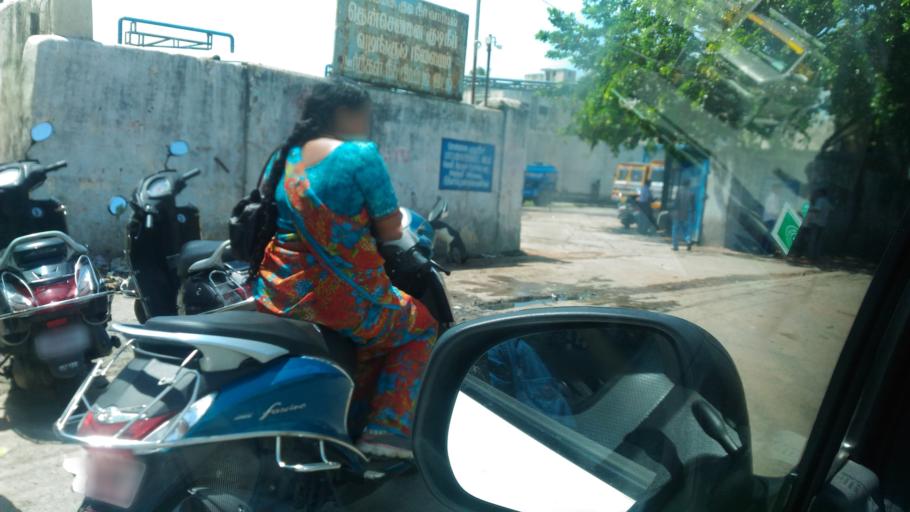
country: IN
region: Tamil Nadu
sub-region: Chennai
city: Chetput
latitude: 13.0524
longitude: 80.2432
